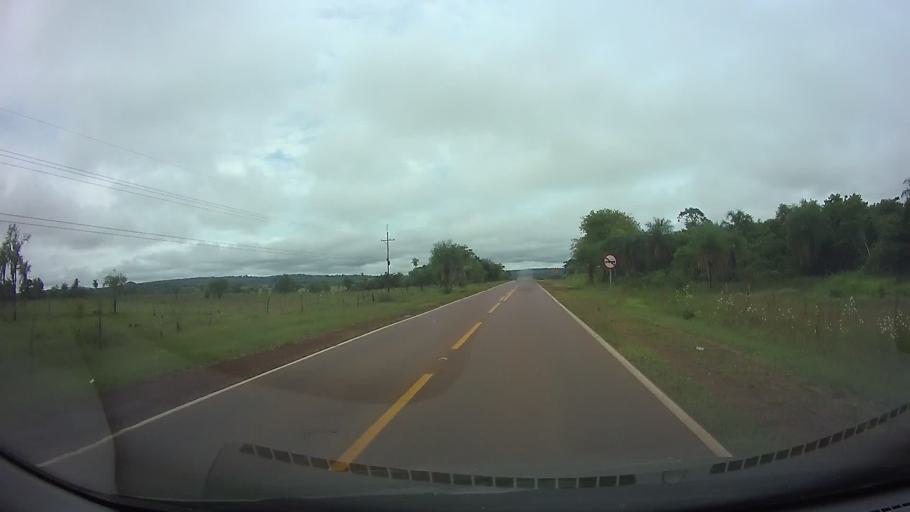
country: PY
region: Paraguari
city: Acahay
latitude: -25.8728
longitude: -57.1251
